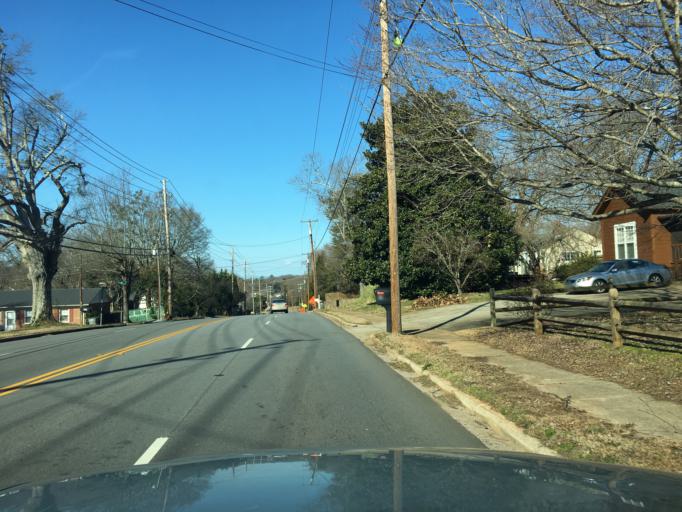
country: US
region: South Carolina
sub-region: Greenville County
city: Sans Souci
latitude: 34.8911
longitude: -82.4188
